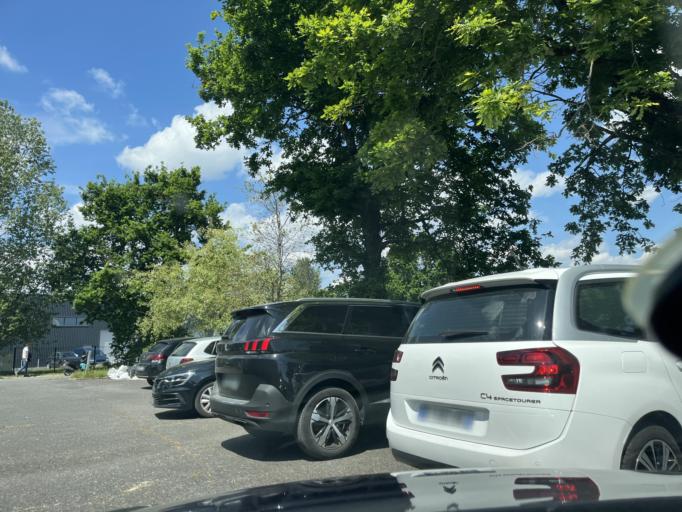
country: FR
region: Aquitaine
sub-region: Departement de la Gironde
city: Le Haillan
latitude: 44.8601
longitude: -0.6813
